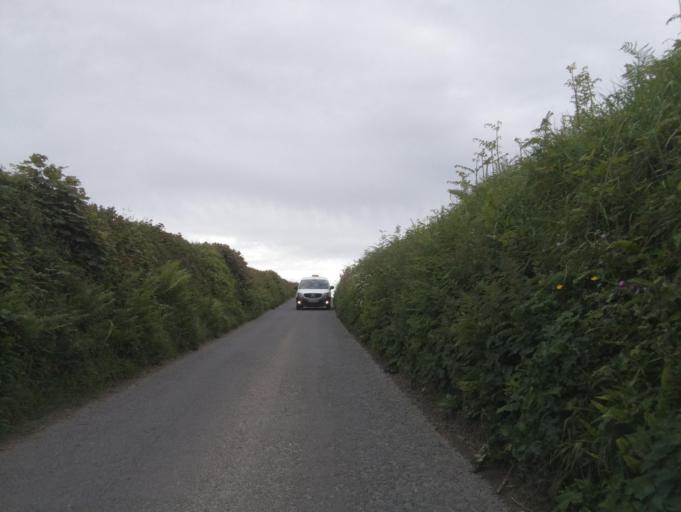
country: GB
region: England
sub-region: Devon
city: Dartmouth
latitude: 50.3299
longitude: -3.6446
